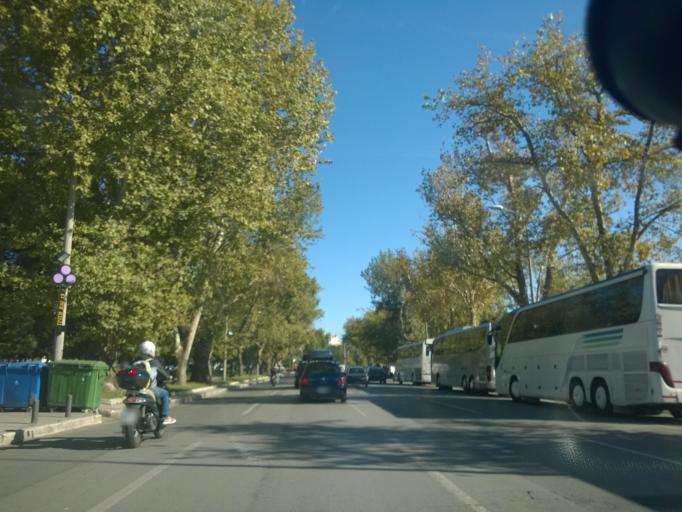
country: GR
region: Central Macedonia
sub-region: Nomos Thessalonikis
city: Agios Pavlos
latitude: 40.6246
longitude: 22.9512
